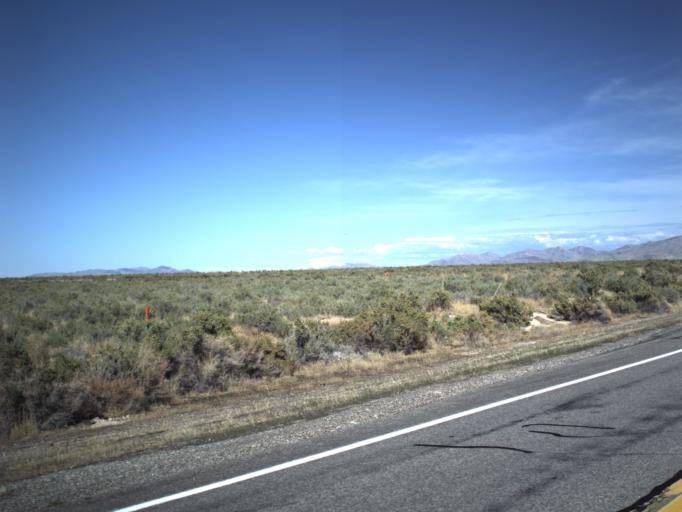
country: US
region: Utah
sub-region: Millard County
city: Delta
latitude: 39.3532
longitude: -112.5051
